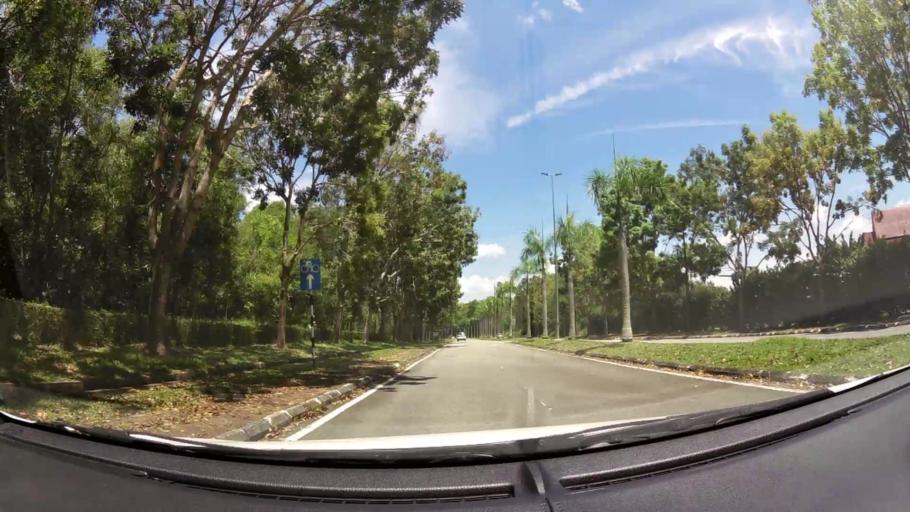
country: BN
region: Brunei and Muara
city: Bandar Seri Begawan
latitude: 4.9229
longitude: 114.9493
